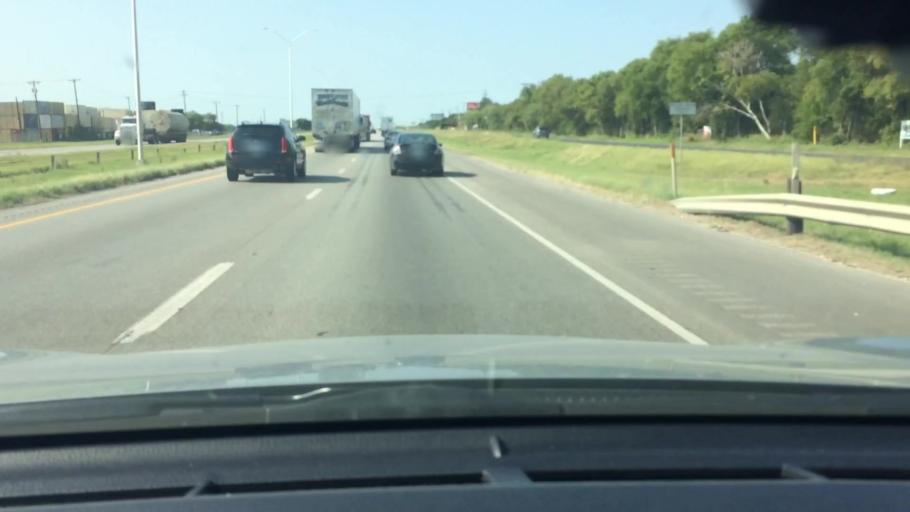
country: US
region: Texas
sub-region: Bexar County
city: China Grove
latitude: 29.3839
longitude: -98.3915
